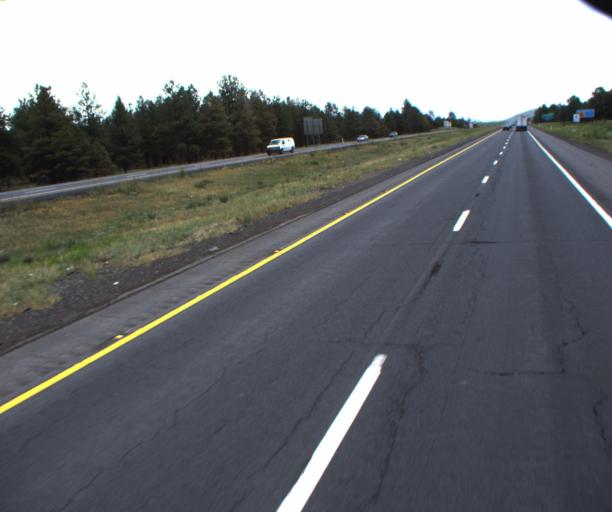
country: US
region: Arizona
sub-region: Coconino County
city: Williams
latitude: 35.2579
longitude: -112.1400
